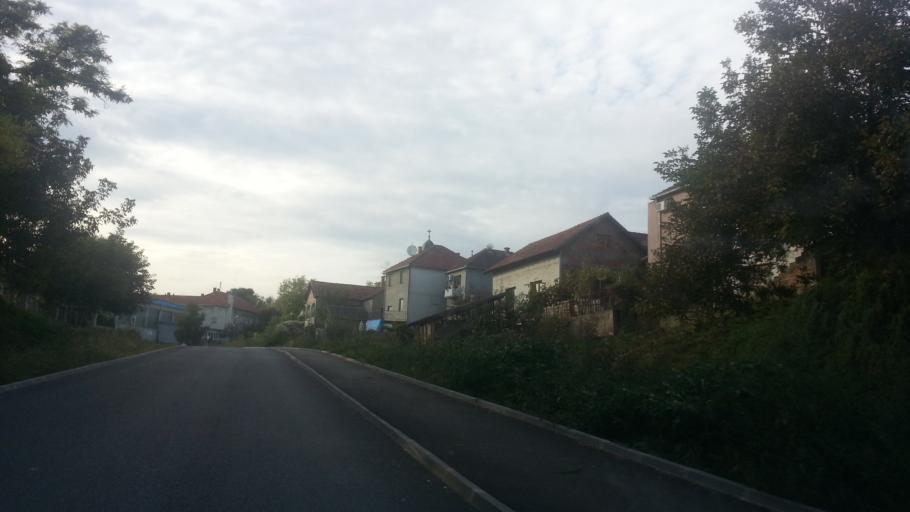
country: RS
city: Belegis
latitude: 45.0180
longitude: 20.3357
